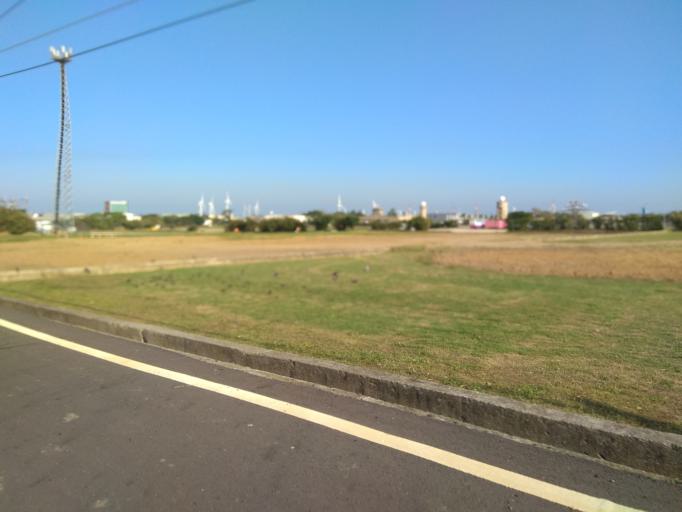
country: TW
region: Taiwan
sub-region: Hsinchu
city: Zhubei
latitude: 25.0034
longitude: 121.0474
